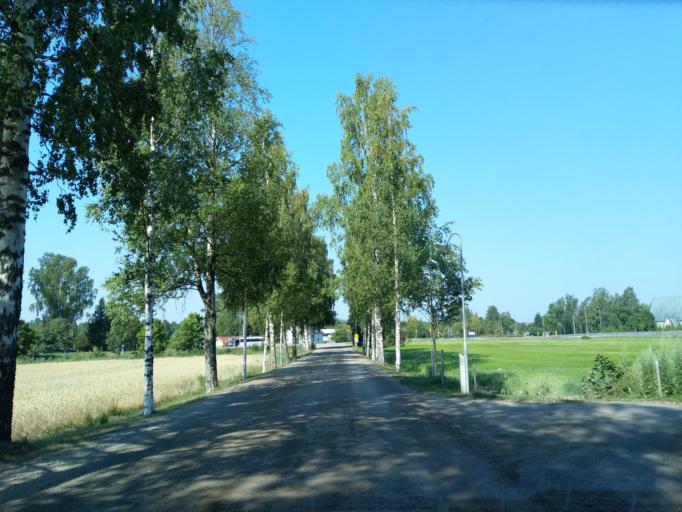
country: FI
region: Satakunta
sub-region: Pori
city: Noormarkku
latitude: 61.5954
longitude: 21.8687
